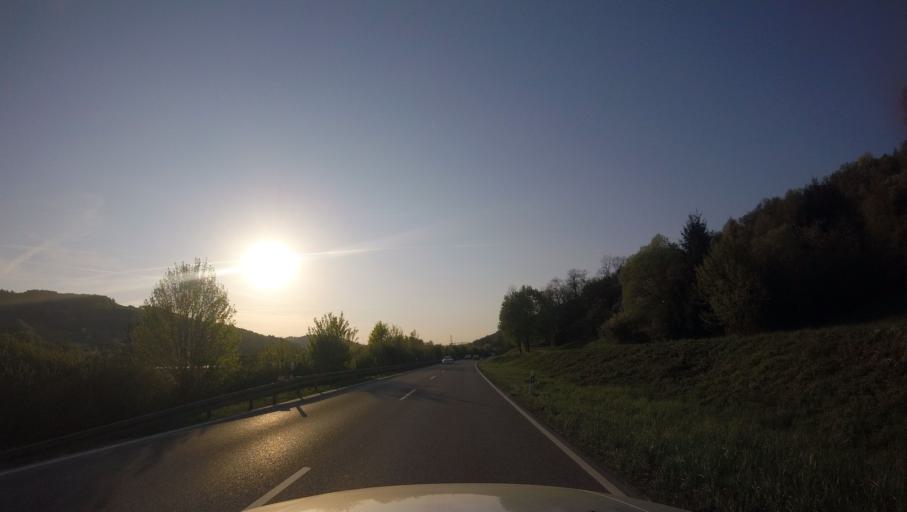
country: DE
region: Baden-Wuerttemberg
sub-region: Regierungsbezirk Stuttgart
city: Murrhardt
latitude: 48.9860
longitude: 9.5622
